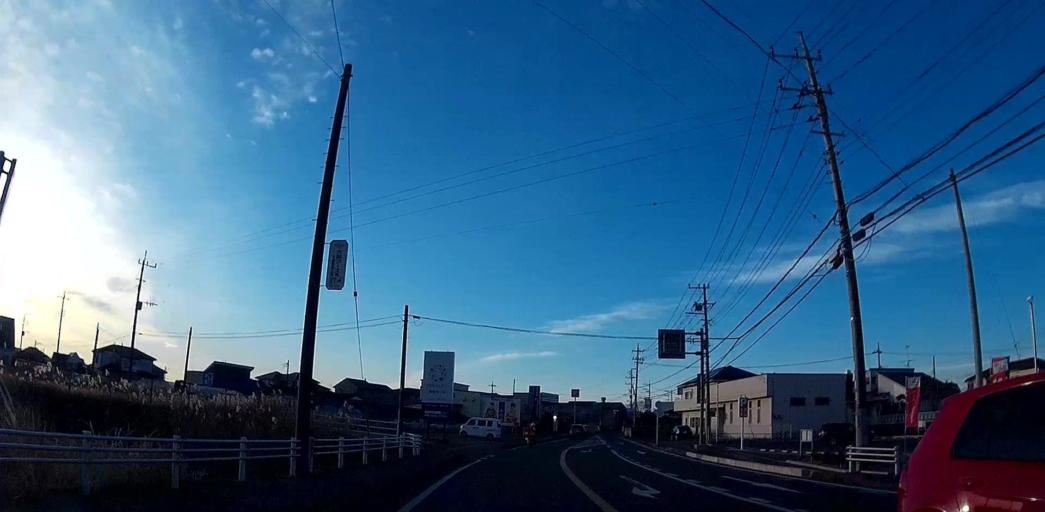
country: JP
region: Chiba
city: Omigawa
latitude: 35.8490
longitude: 140.6138
